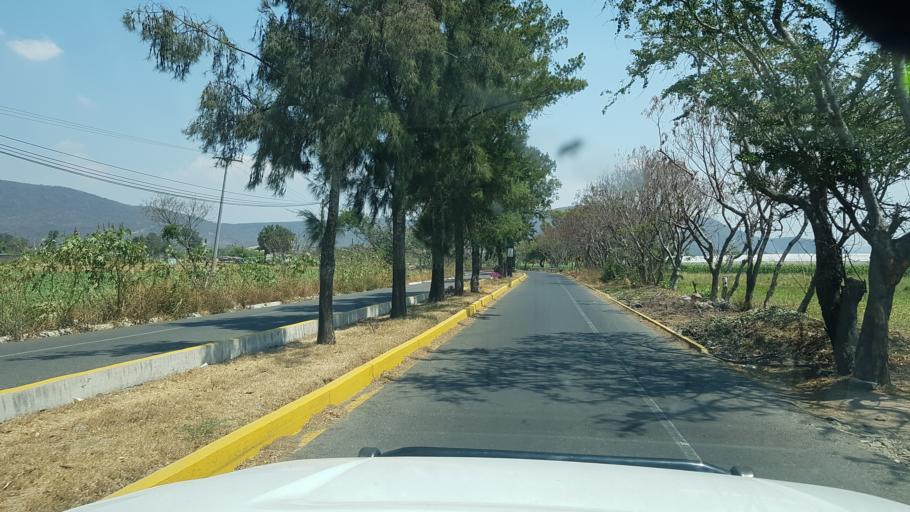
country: MX
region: Puebla
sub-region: Huaquechula
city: Cacaloxuchitl
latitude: 18.7909
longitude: -98.4619
